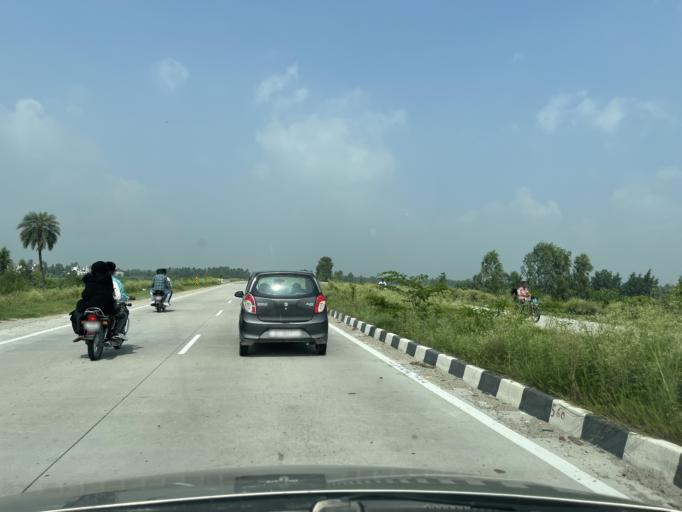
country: IN
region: Uttarakhand
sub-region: Udham Singh Nagar
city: Kashipur
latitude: 29.1640
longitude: 78.9929
